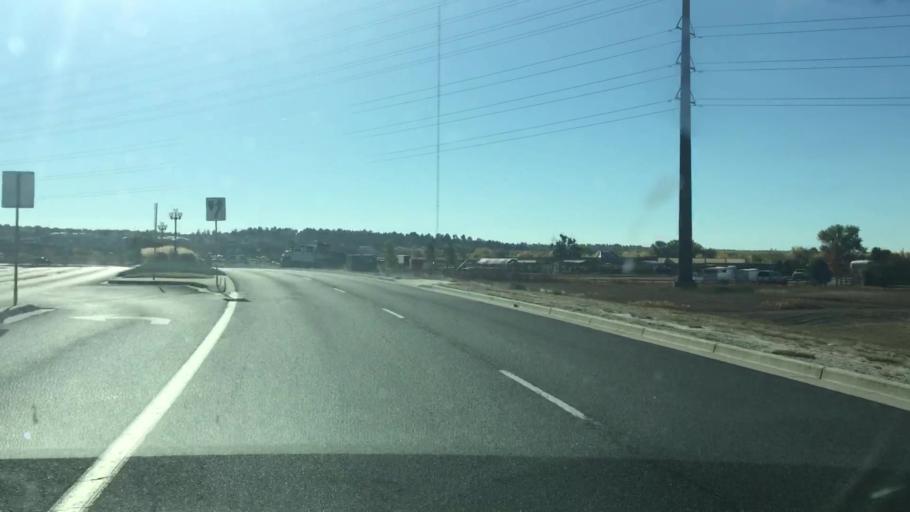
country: US
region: Colorado
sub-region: Douglas County
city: Parker
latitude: 39.5117
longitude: -104.7732
